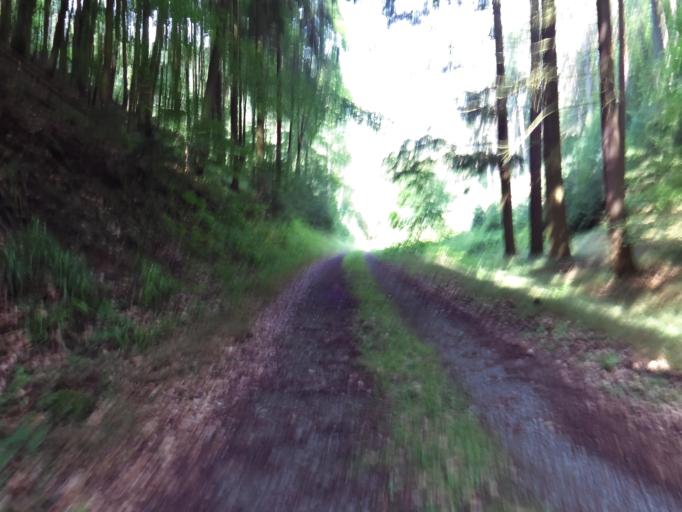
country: DE
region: Rheinland-Pfalz
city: Neidenfels
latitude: 49.4261
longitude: 8.0653
